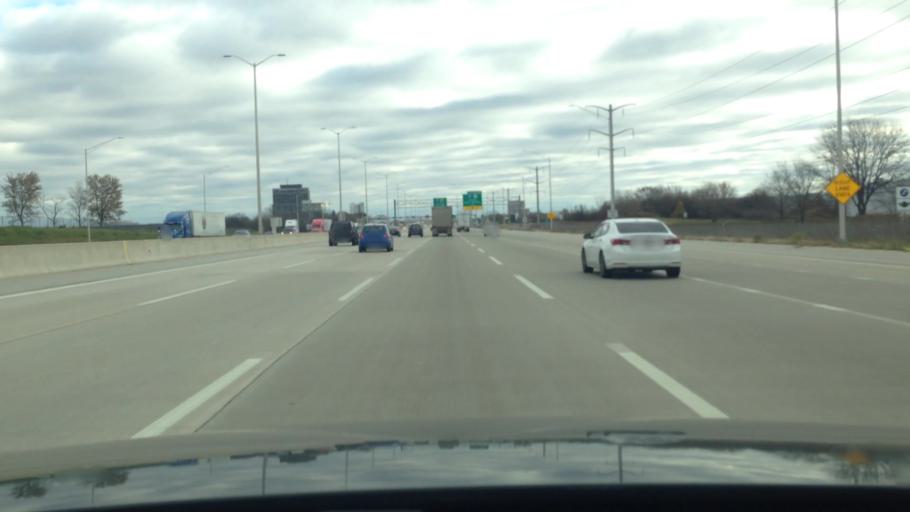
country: US
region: Illinois
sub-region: Cook County
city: Hoffman Estates
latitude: 42.0624
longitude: -88.0685
